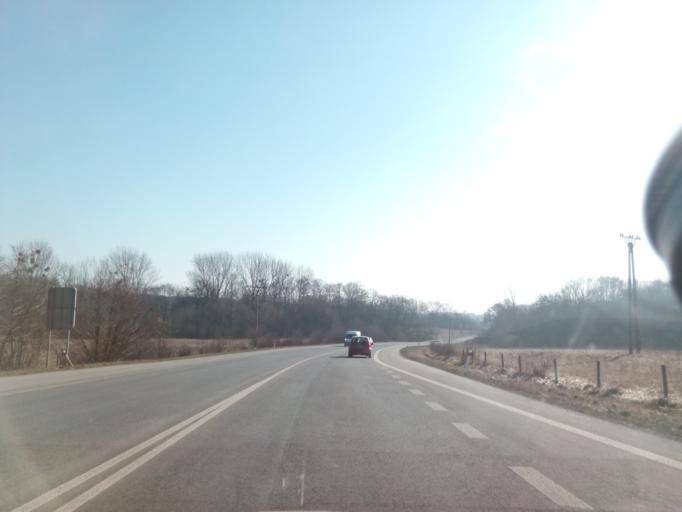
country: SK
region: Kosicky
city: Secovce
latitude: 48.7358
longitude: 21.5680
